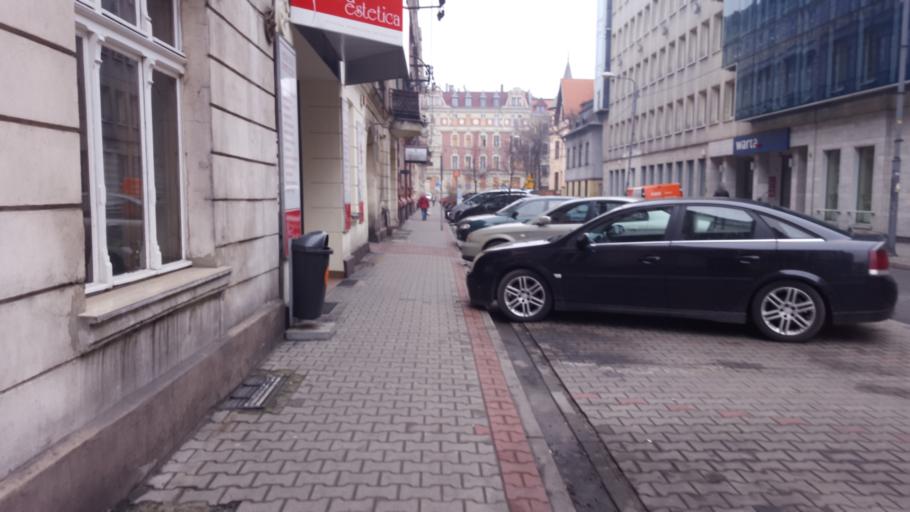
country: PL
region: Silesian Voivodeship
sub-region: Katowice
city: Katowice
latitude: 50.2622
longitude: 19.0140
